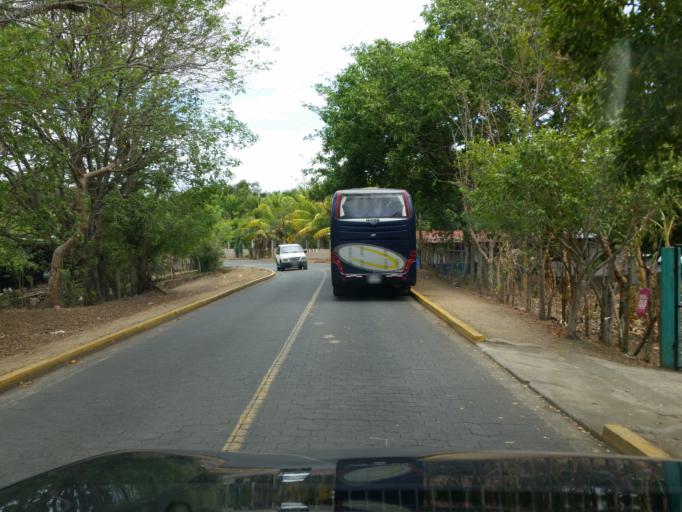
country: NI
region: Masaya
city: Masaya
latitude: 11.9815
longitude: -86.0616
